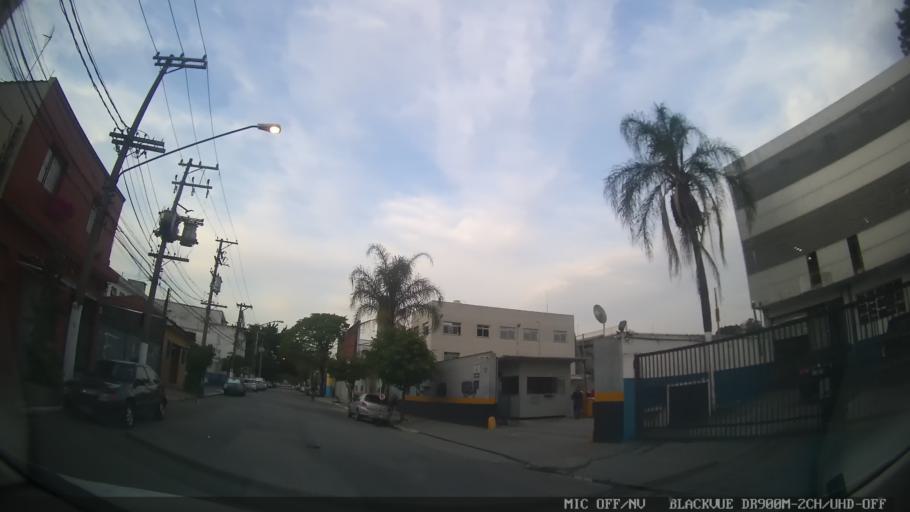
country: BR
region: Sao Paulo
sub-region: Sao Caetano Do Sul
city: Sao Caetano do Sul
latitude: -23.6027
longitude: -46.5895
